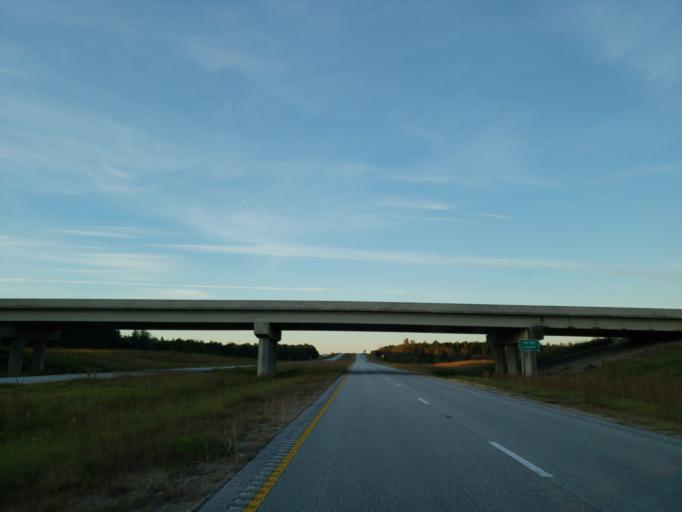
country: US
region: Mississippi
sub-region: Wayne County
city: Belmont
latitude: 31.4356
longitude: -88.4655
